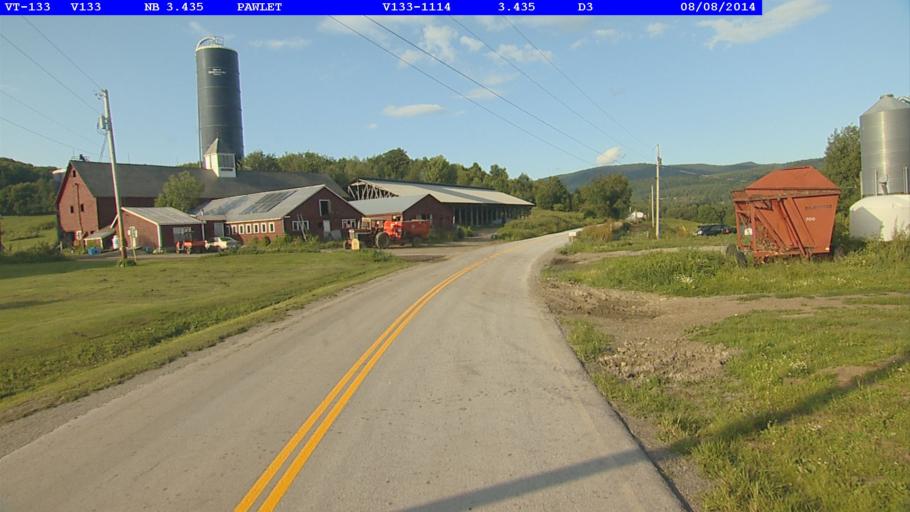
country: US
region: New York
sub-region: Washington County
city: Granville
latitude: 43.3802
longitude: -73.1406
